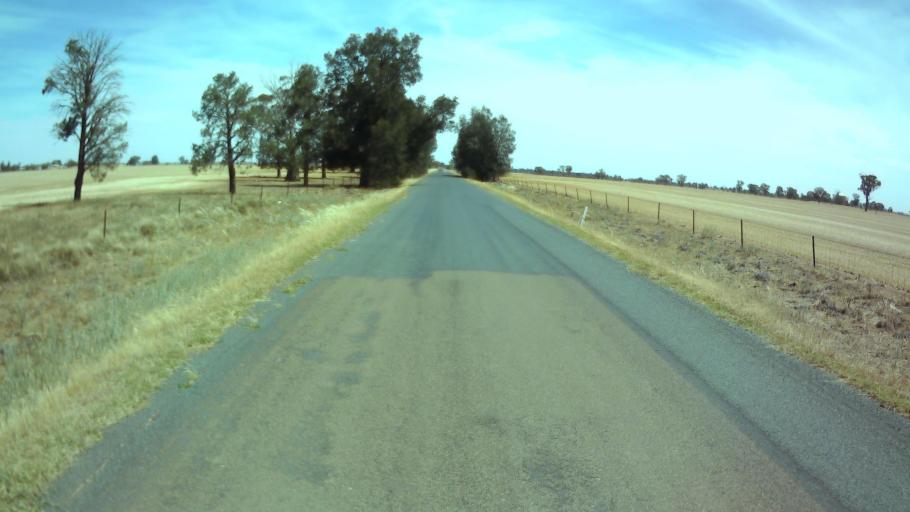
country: AU
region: New South Wales
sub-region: Weddin
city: Grenfell
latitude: -33.9283
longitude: 147.7628
